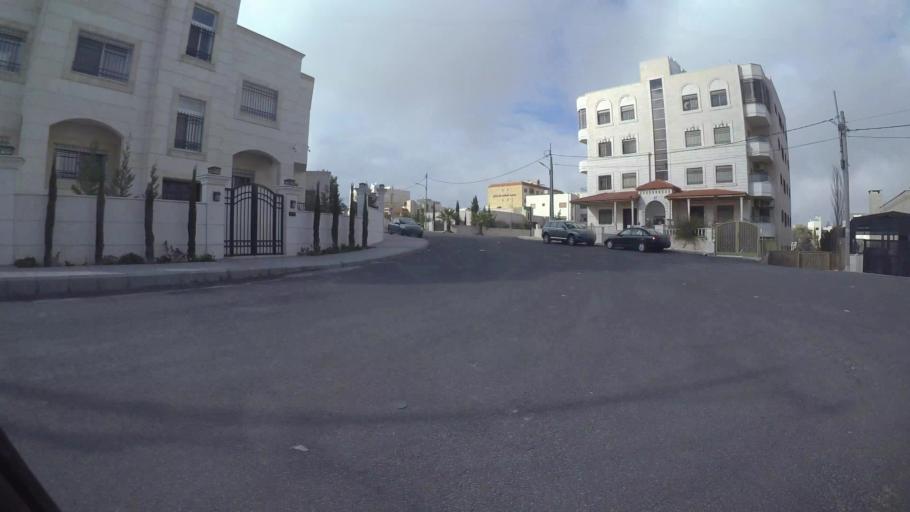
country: JO
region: Amman
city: Al Jubayhah
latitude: 32.0403
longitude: 35.8698
